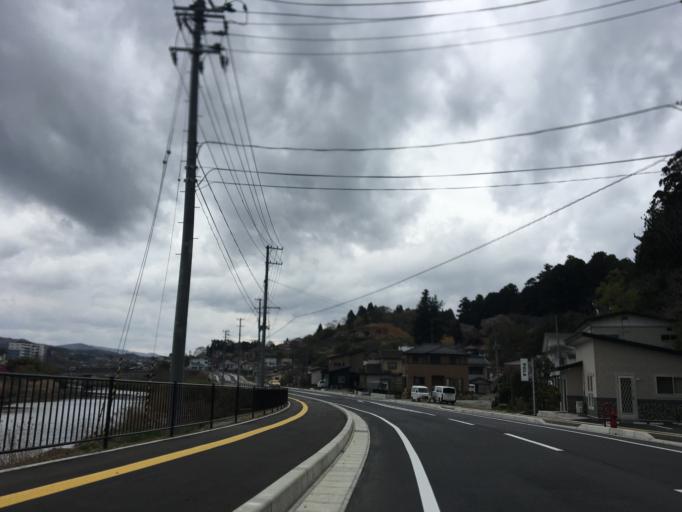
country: JP
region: Iwate
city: Ofunato
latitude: 38.9003
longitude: 141.5683
